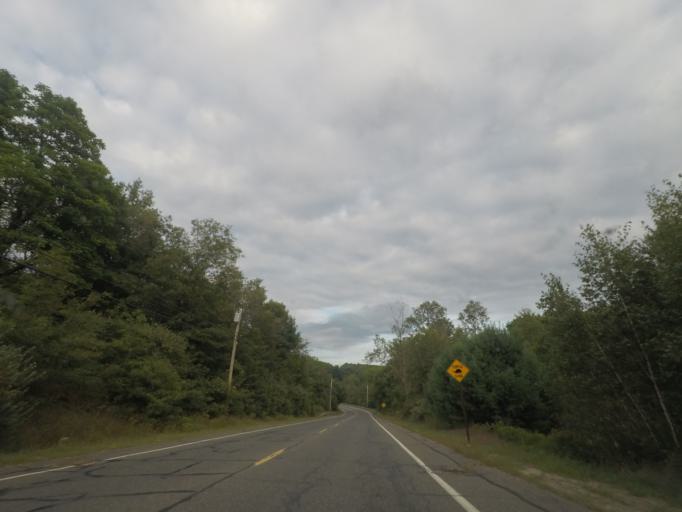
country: US
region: Massachusetts
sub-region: Hampden County
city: Palmer
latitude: 42.1909
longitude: -72.2878
